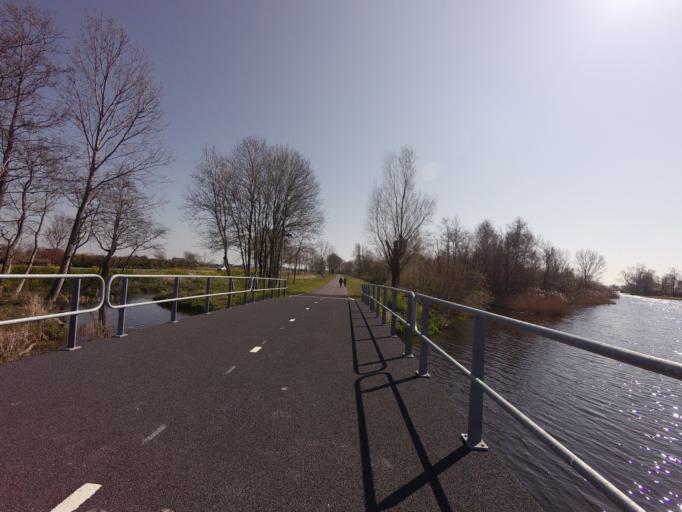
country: NL
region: South Holland
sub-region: Gemeente Alphen aan den Rijn
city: Alphen aan den Rijn
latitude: 52.1330
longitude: 4.7034
